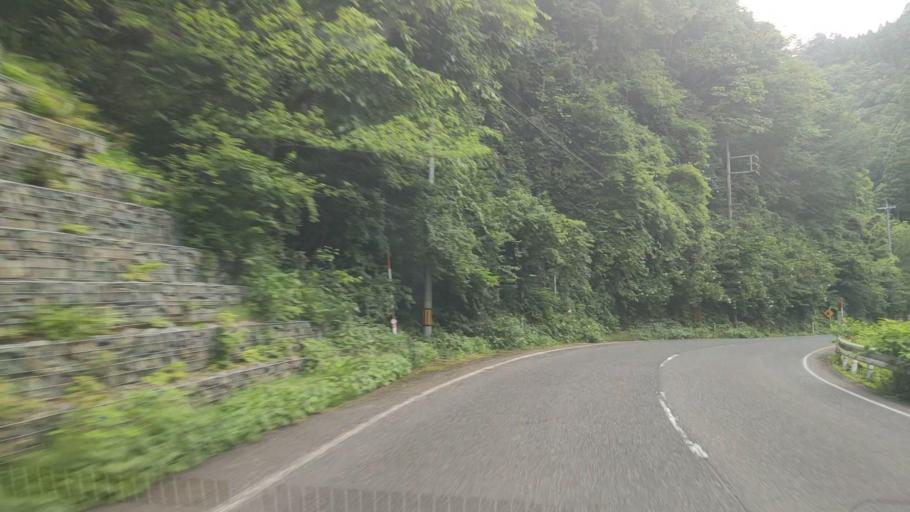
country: JP
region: Tottori
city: Tottori
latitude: 35.3332
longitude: 134.0674
